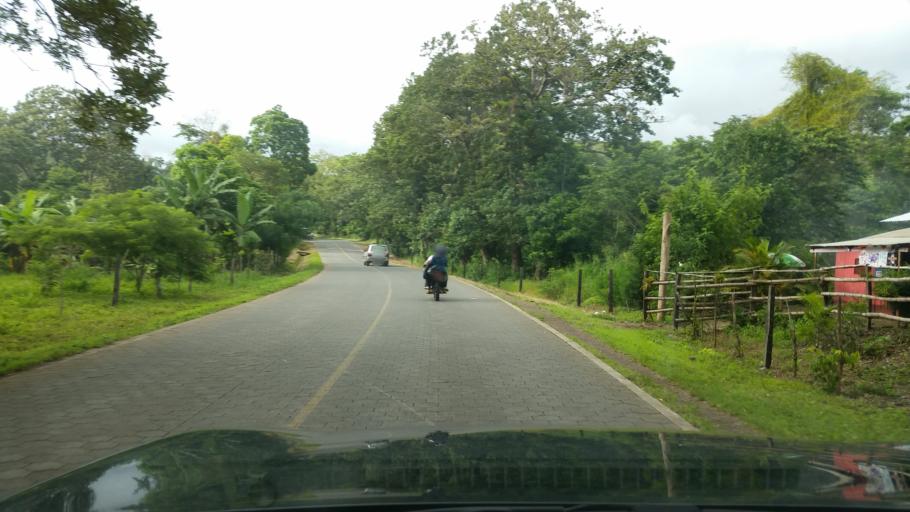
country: NI
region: Matagalpa
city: San Ramon
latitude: 13.1588
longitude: -85.7309
